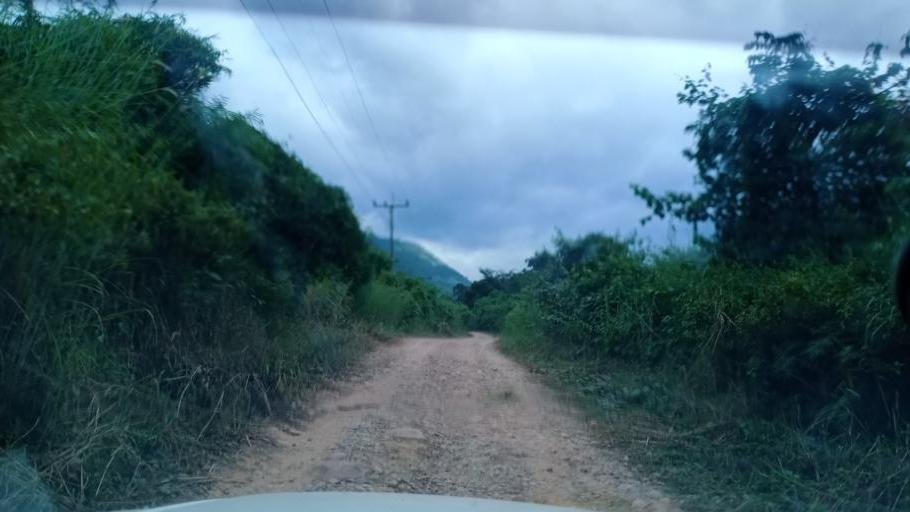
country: TH
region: Changwat Bueng Kan
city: Pak Khat
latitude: 18.7248
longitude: 103.2405
